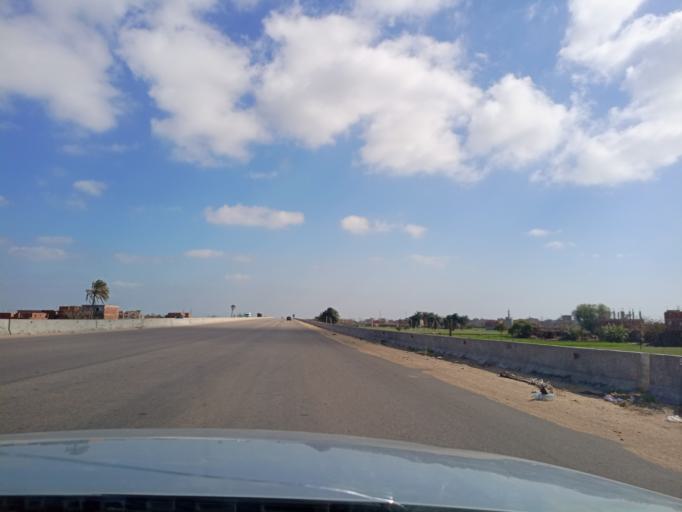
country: EG
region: Muhafazat al Minufiyah
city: Al Bajur
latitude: 30.3997
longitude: 31.0223
